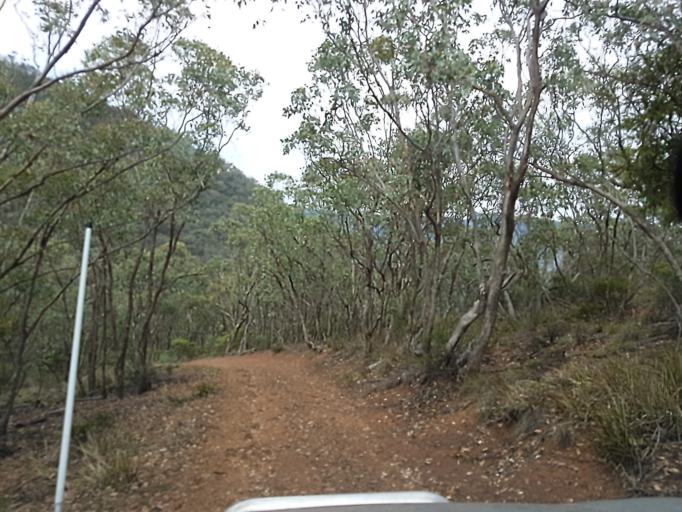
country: AU
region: New South Wales
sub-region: Snowy River
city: Jindabyne
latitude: -36.9947
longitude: 148.4083
